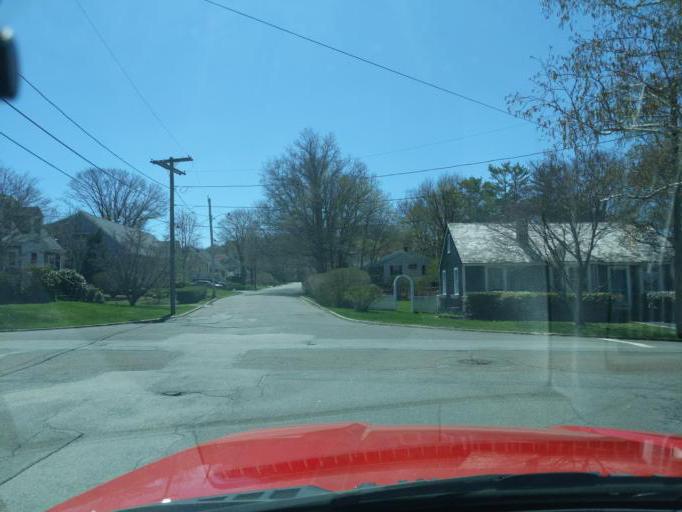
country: US
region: Massachusetts
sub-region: Essex County
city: Rockport
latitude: 42.6566
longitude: -70.6069
